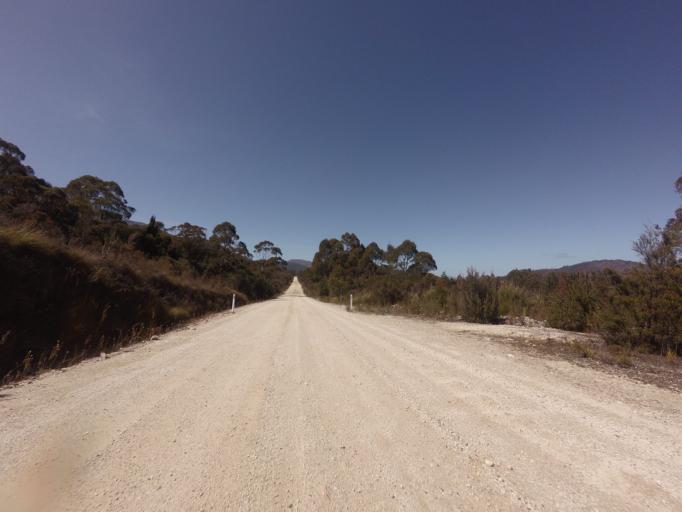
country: AU
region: Tasmania
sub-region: Huon Valley
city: Geeveston
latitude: -42.9442
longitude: 146.3497
